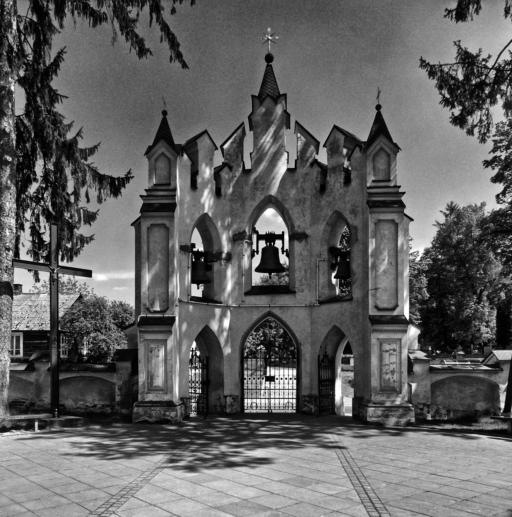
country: PL
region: Lublin Voivodeship
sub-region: Powiat lubelski
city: Lublin
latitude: 51.1950
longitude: 22.5956
